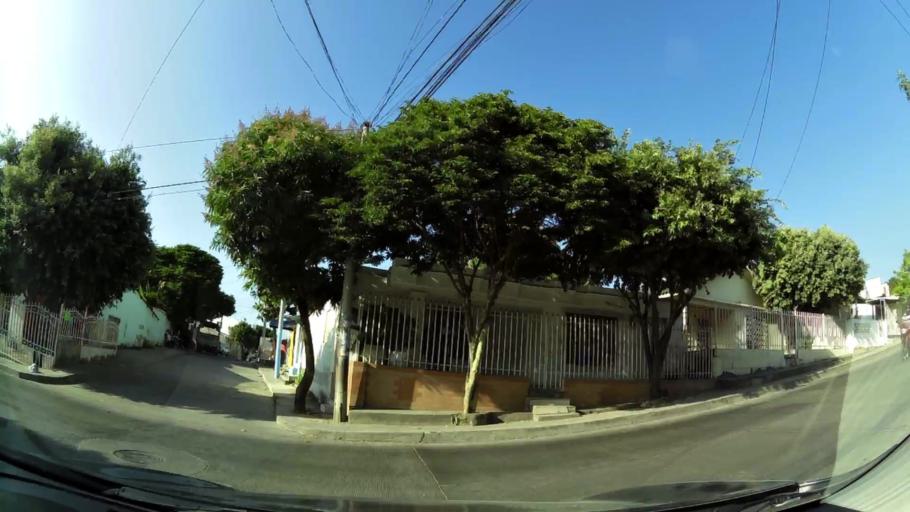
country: CO
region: Bolivar
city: Cartagena
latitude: 10.4028
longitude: -75.4860
